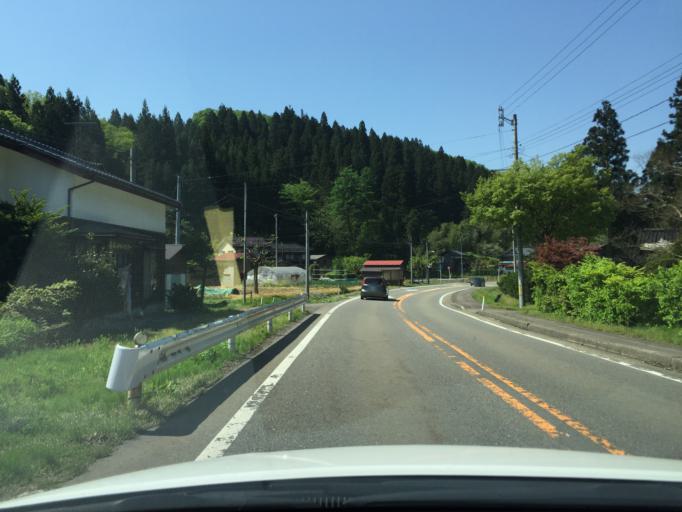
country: JP
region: Niigata
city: Kamo
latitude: 37.6363
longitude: 139.1093
